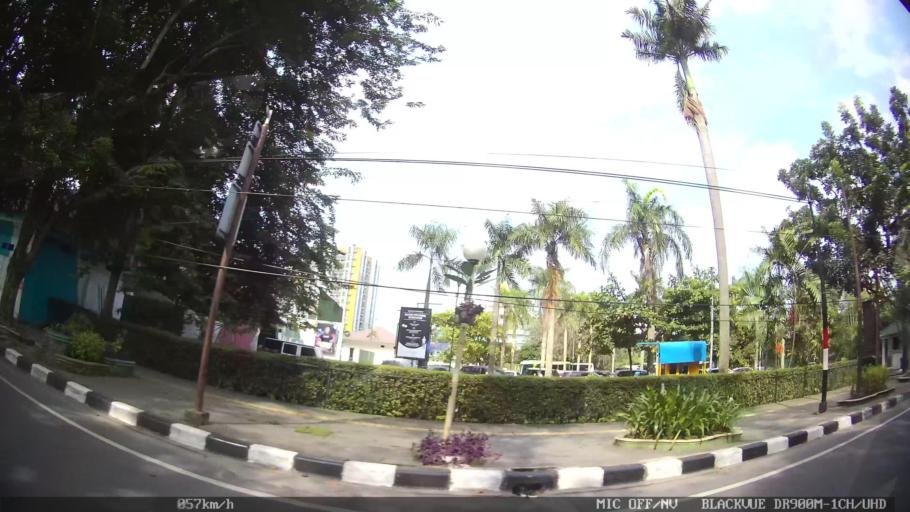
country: ID
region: North Sumatra
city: Medan
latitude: 3.5825
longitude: 98.6760
